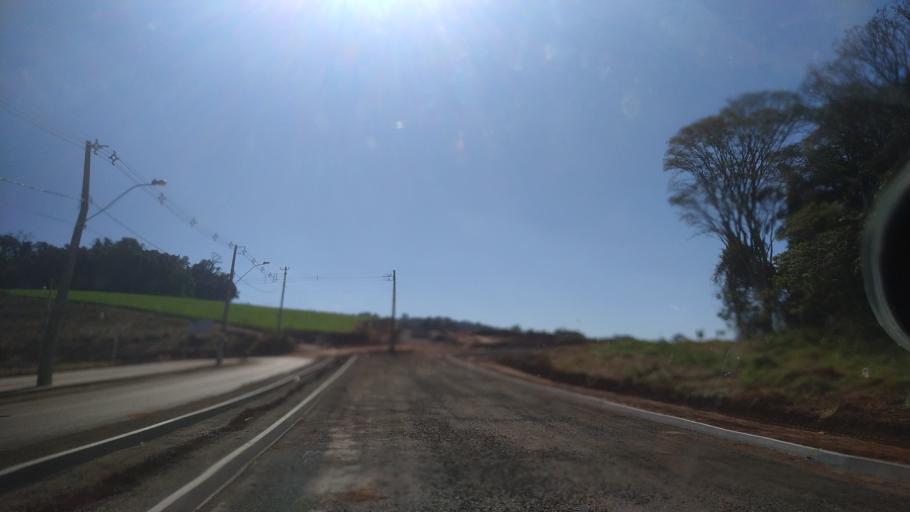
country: BR
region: Santa Catarina
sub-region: Chapeco
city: Chapeco
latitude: -27.0857
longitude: -52.6915
